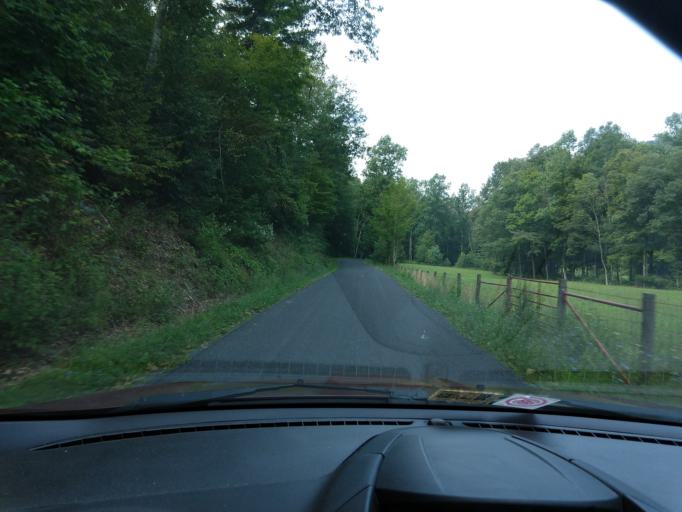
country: US
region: Virginia
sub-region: City of Covington
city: Covington
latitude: 37.9031
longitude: -80.0821
